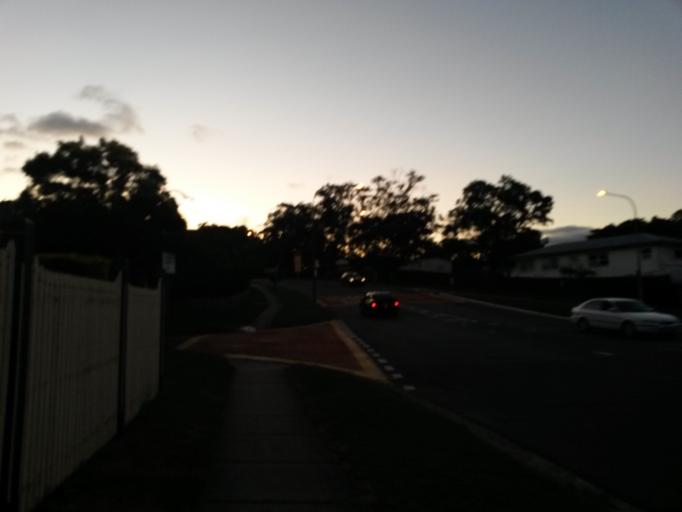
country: AU
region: Queensland
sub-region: Brisbane
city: Camp Hill
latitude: -27.5031
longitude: 153.0860
